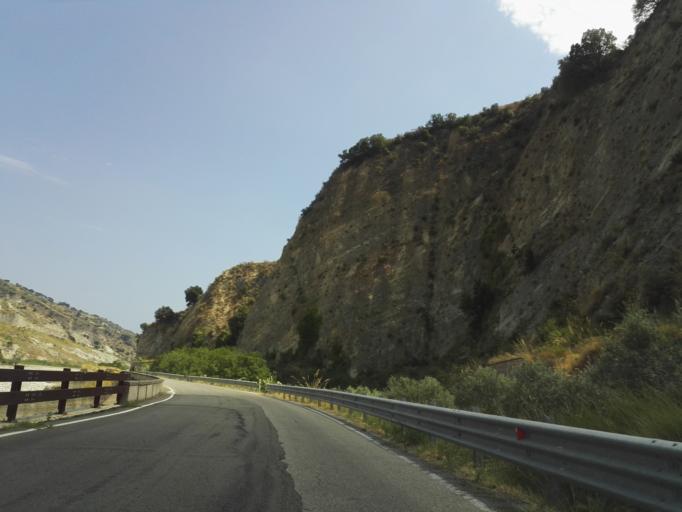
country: IT
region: Calabria
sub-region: Provincia di Reggio Calabria
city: Stilo
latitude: 38.4831
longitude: 16.4750
